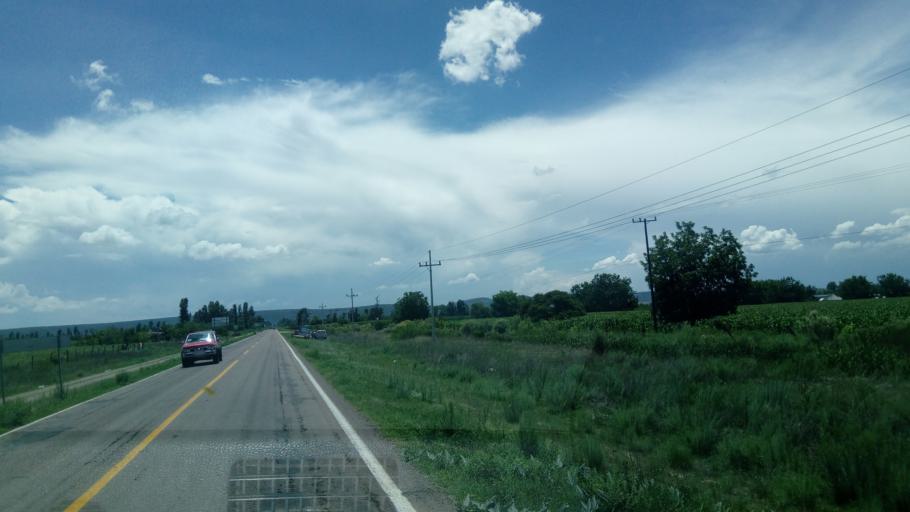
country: MX
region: Durango
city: Victoria de Durango
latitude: 24.1799
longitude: -104.5496
